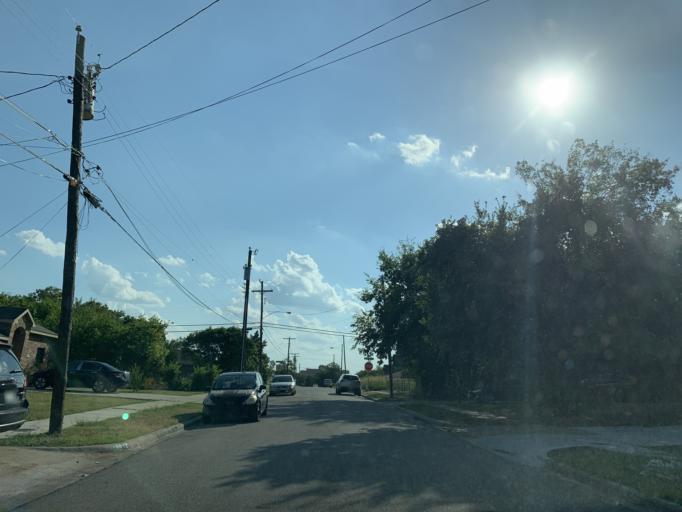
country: US
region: Texas
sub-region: Dallas County
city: Hutchins
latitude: 32.6986
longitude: -96.7804
